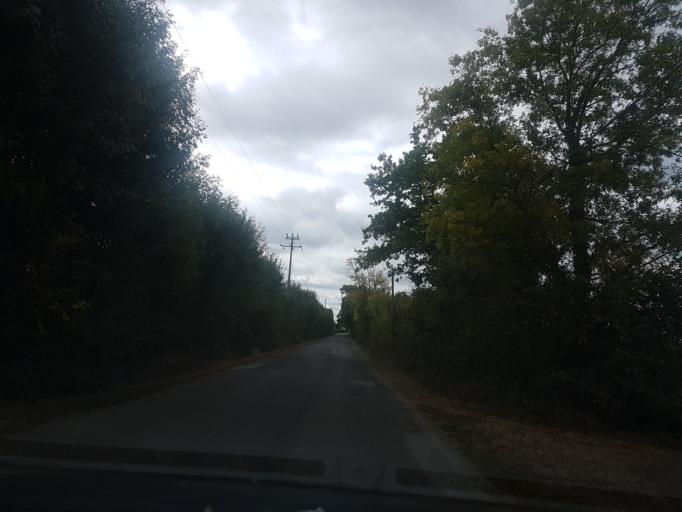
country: FR
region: Pays de la Loire
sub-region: Departement de la Loire-Atlantique
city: Ligne
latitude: 47.4079
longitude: -1.3838
